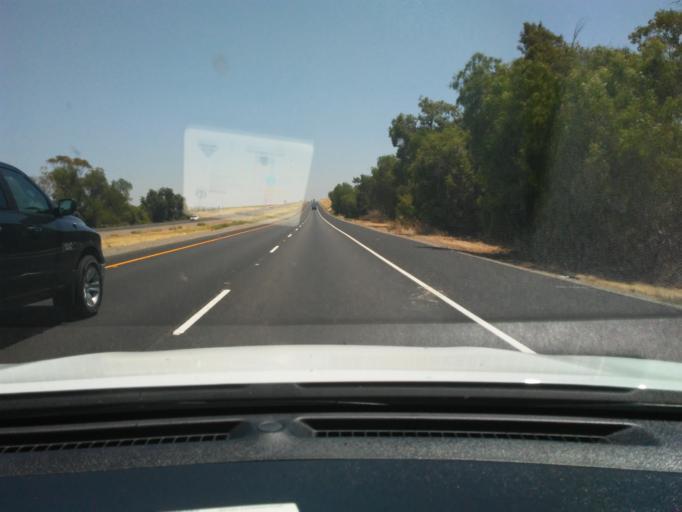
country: US
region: California
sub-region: San Joaquin County
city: Tracy
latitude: 37.6311
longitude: -121.3898
